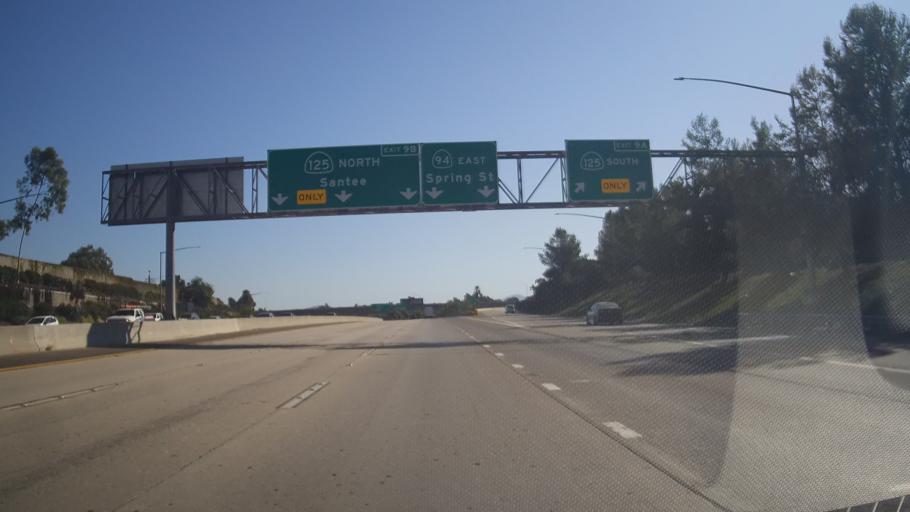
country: US
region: California
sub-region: San Diego County
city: Lemon Grove
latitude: 32.7476
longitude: -117.0243
